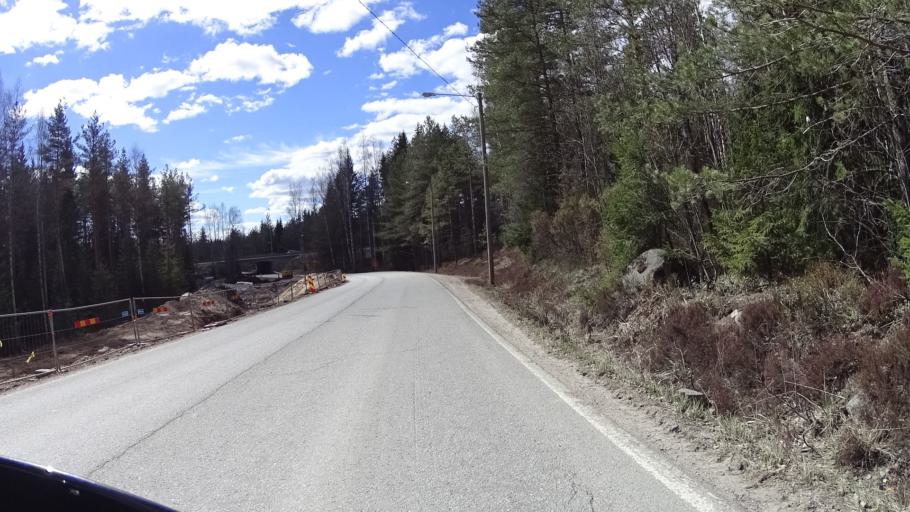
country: FI
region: Uusimaa
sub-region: Helsinki
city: Espoo
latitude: 60.2550
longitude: 24.5249
